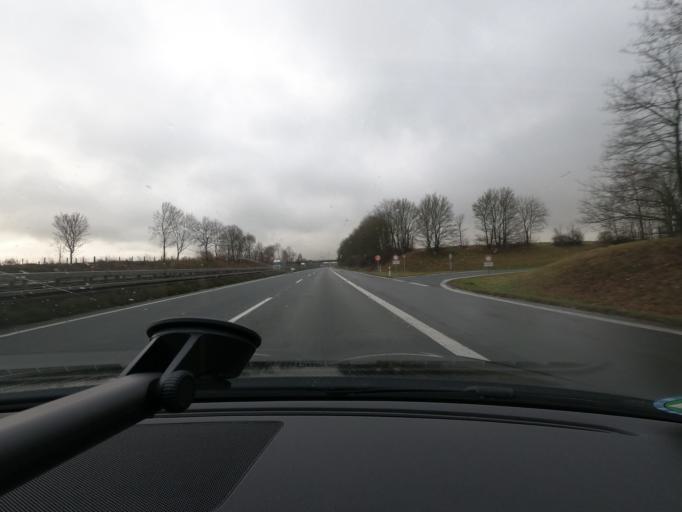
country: DE
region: North Rhine-Westphalia
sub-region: Regierungsbezirk Detmold
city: Wunnenberg
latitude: 51.5752
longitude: 8.7323
